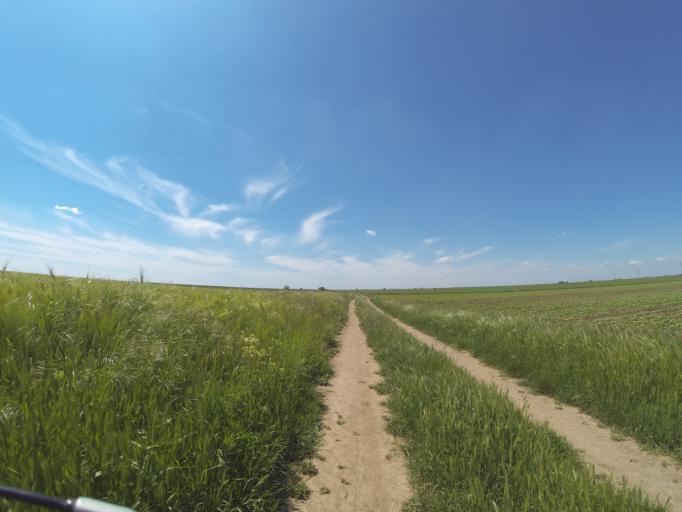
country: RO
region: Dolj
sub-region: Comuna Leu
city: Leu
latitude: 44.2113
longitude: 24.0324
